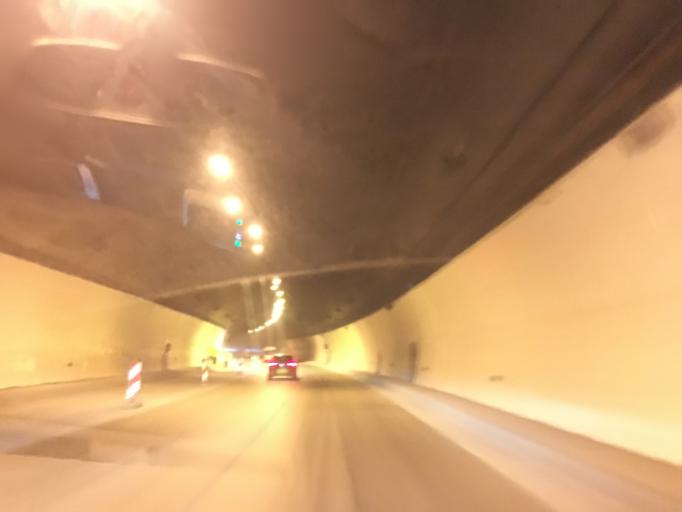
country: DZ
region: Bouira
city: Draa el Mizan
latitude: 36.4450
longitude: 3.7887
